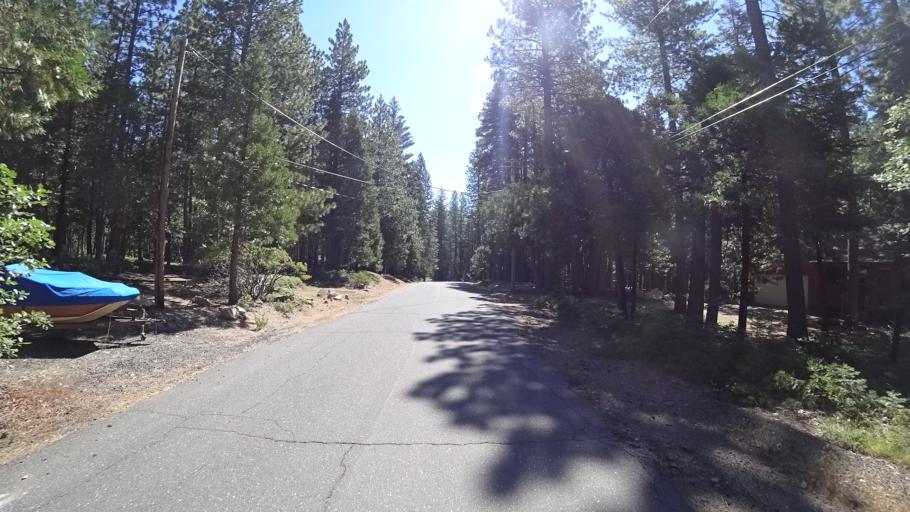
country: US
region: California
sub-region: Calaveras County
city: Arnold
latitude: 38.2799
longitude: -120.2829
